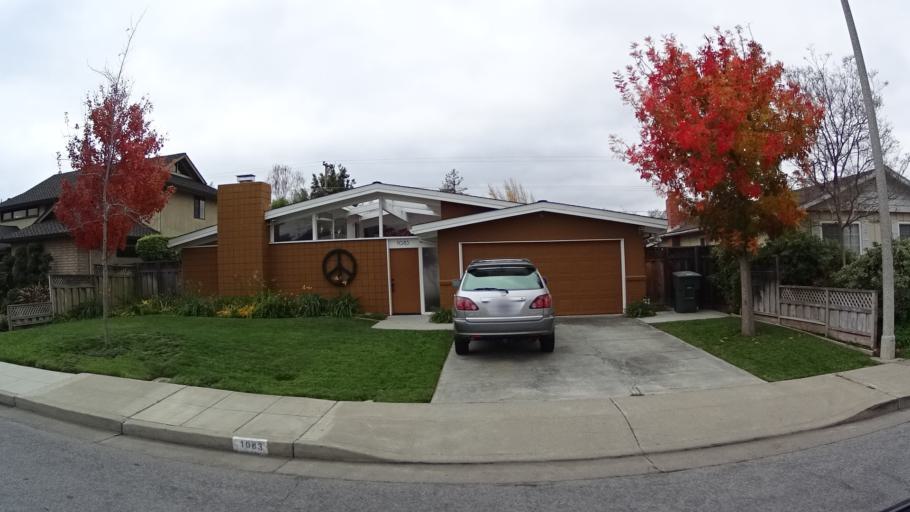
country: US
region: California
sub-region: Santa Clara County
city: Sunnyvale
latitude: 37.3556
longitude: -122.0219
